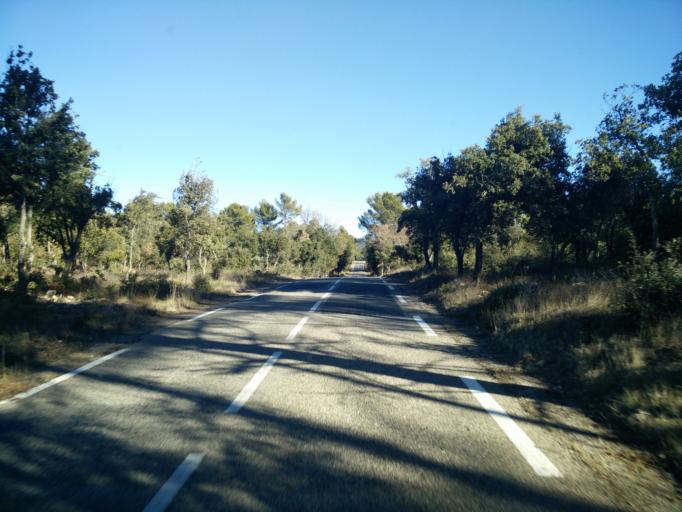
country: FR
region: Provence-Alpes-Cote d'Azur
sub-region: Departement du Var
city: Aups
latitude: 43.6042
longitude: 6.2029
